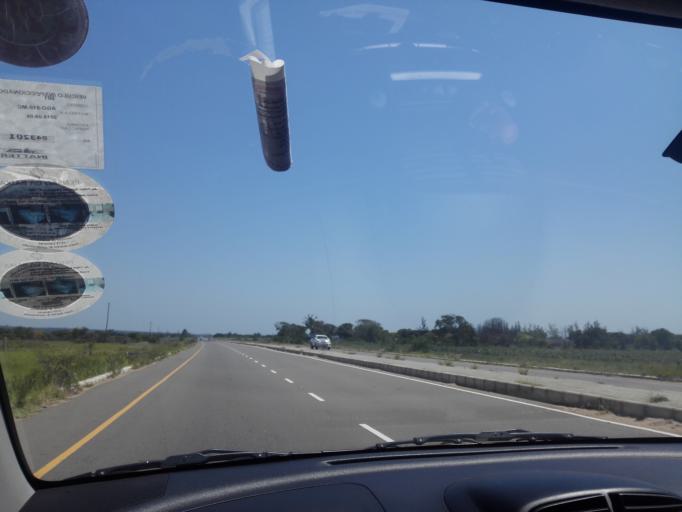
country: MZ
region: Maputo City
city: Maputo
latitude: -25.8031
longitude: 32.6730
